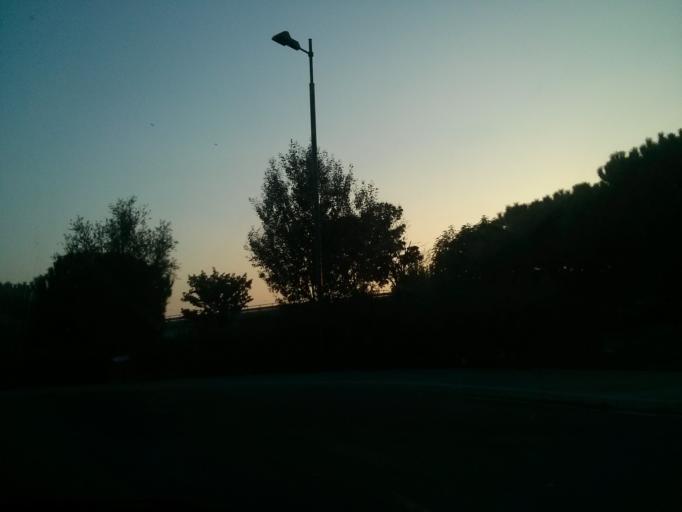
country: FR
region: Languedoc-Roussillon
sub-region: Departement du Gard
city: Gallargues-le-Montueux
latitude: 43.7180
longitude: 4.1837
